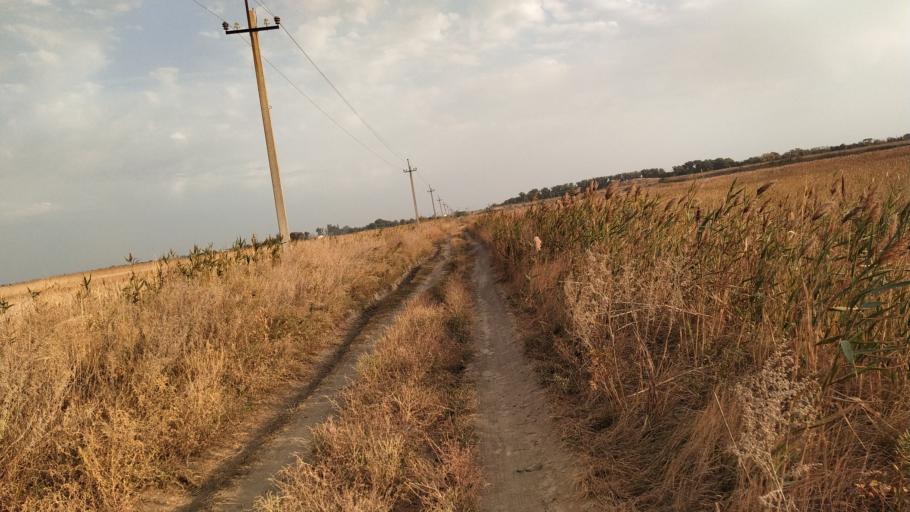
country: RU
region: Rostov
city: Kuleshovka
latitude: 47.1142
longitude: 39.6052
